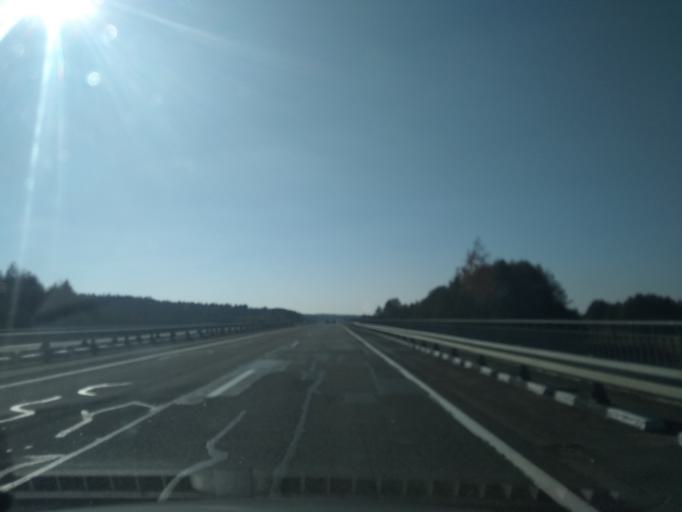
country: BY
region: Brest
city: Ivatsevichy
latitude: 52.7896
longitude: 25.5582
